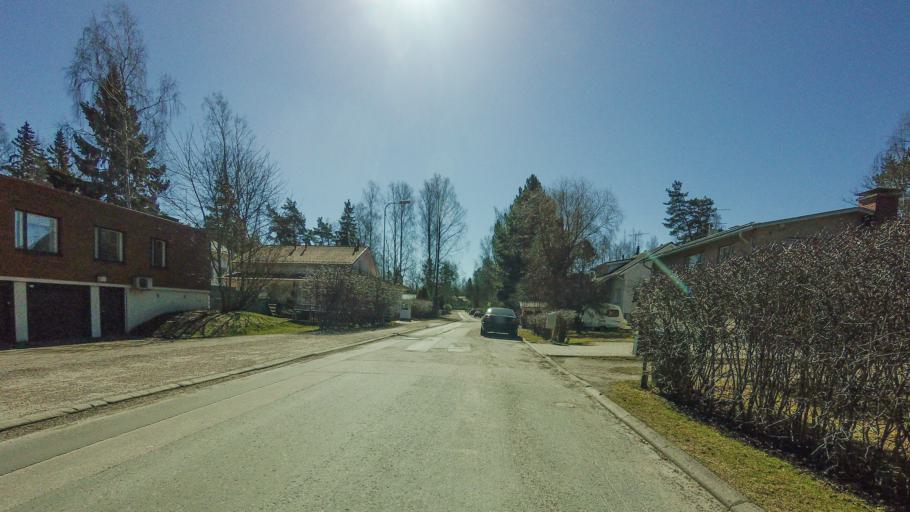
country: FI
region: Uusimaa
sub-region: Helsinki
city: Helsinki
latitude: 60.1734
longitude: 25.0423
